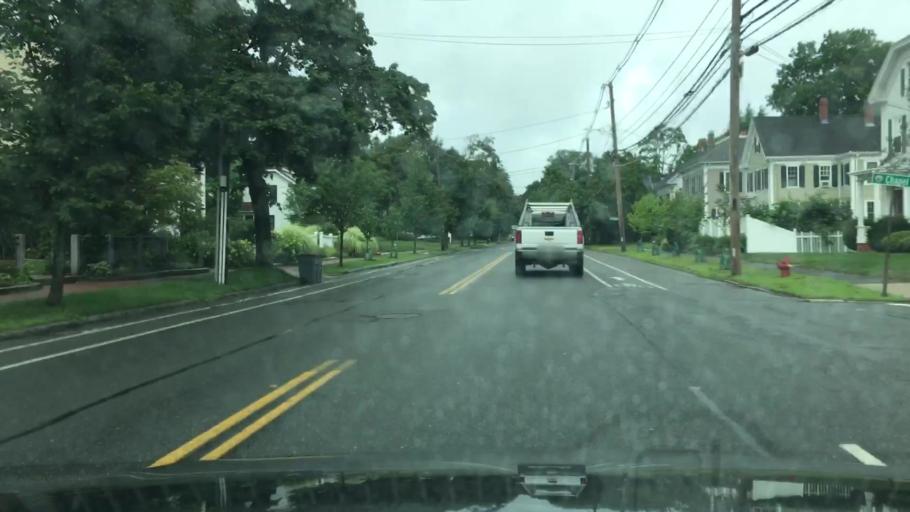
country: US
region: Massachusetts
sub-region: Essex County
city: Newburyport
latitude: 42.8186
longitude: -70.8903
